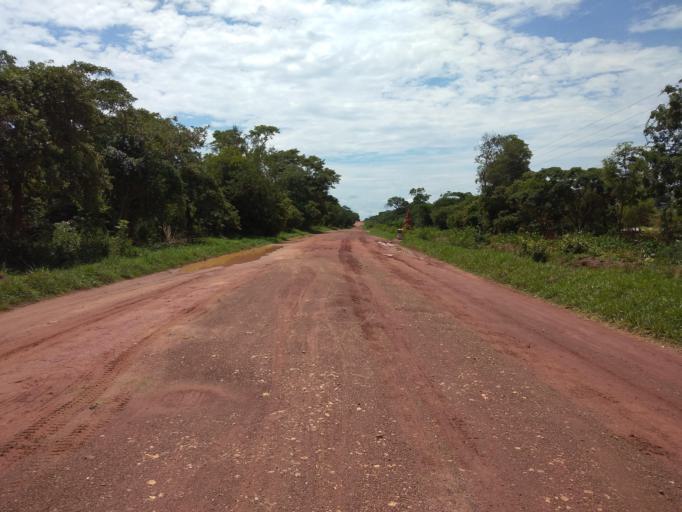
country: ZM
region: Copperbelt
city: Luanshya
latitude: -13.4829
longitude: 28.7216
